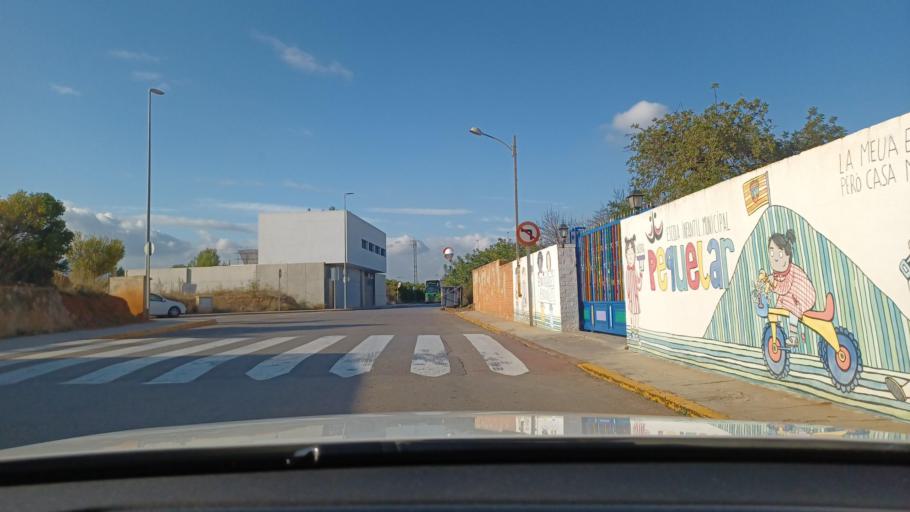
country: ES
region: Valencia
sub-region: Provincia de Castello
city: Betxi
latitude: 39.9319
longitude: -0.2016
